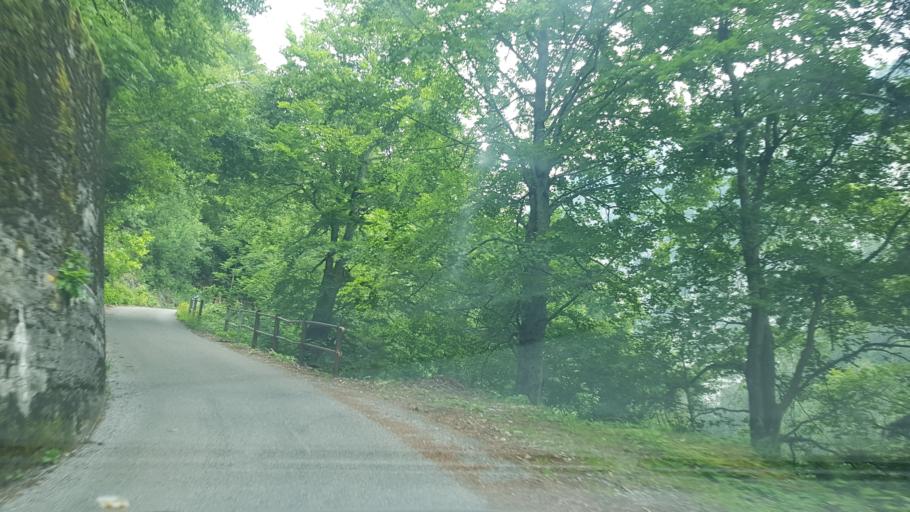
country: IT
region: Friuli Venezia Giulia
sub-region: Provincia di Udine
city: Paularo
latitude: 46.5791
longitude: 13.1334
